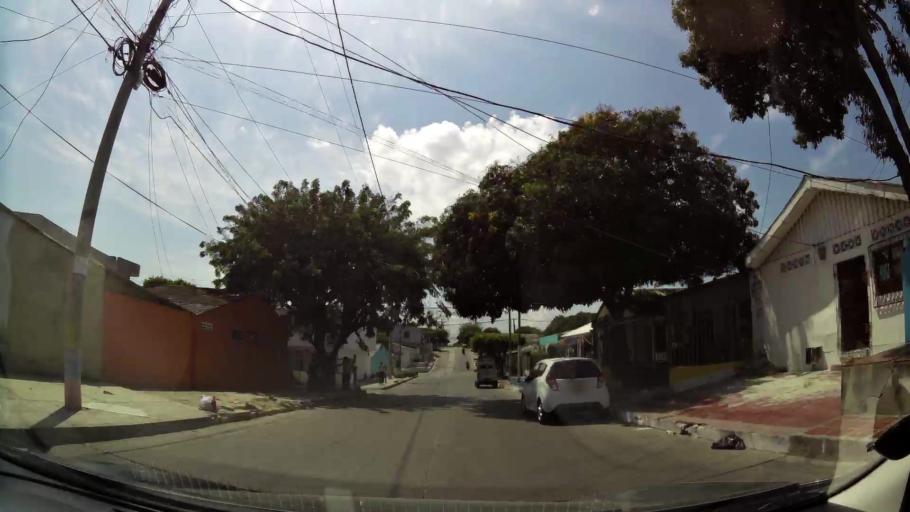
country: CO
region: Atlantico
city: Barranquilla
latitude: 10.9596
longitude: -74.8071
